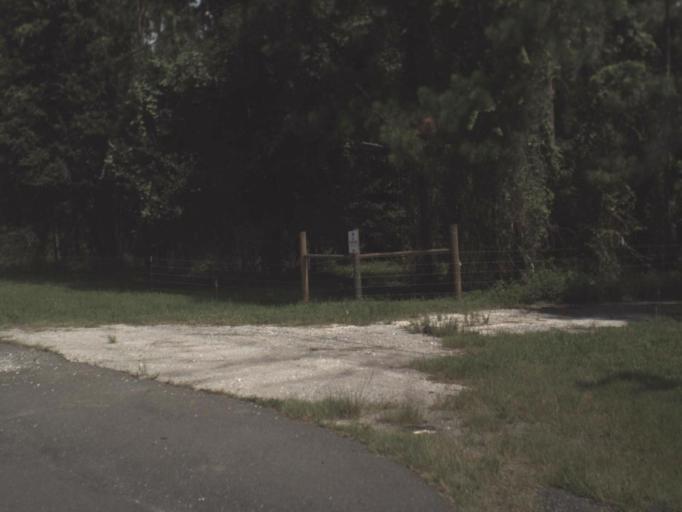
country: US
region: Florida
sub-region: Pasco County
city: Shady Hills
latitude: 28.3250
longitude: -82.5249
